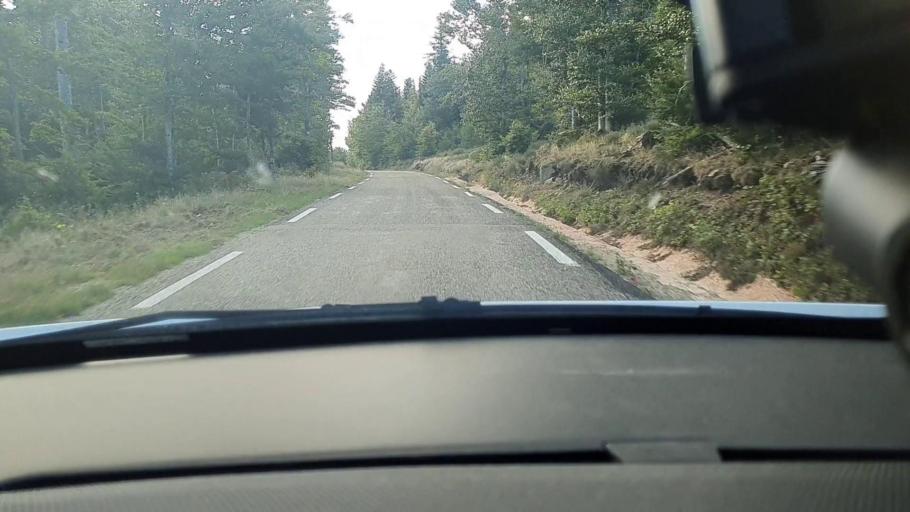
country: FR
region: Languedoc-Roussillon
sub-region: Departement du Gard
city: Branoux-les-Taillades
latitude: 44.3716
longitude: 3.9142
